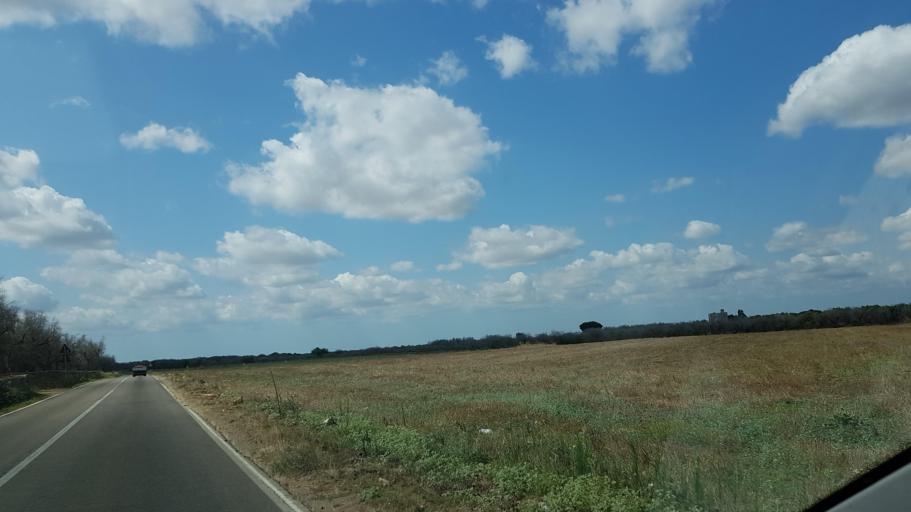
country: IT
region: Apulia
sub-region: Provincia di Brindisi
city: Torchiarolo
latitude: 40.4685
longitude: 18.0605
